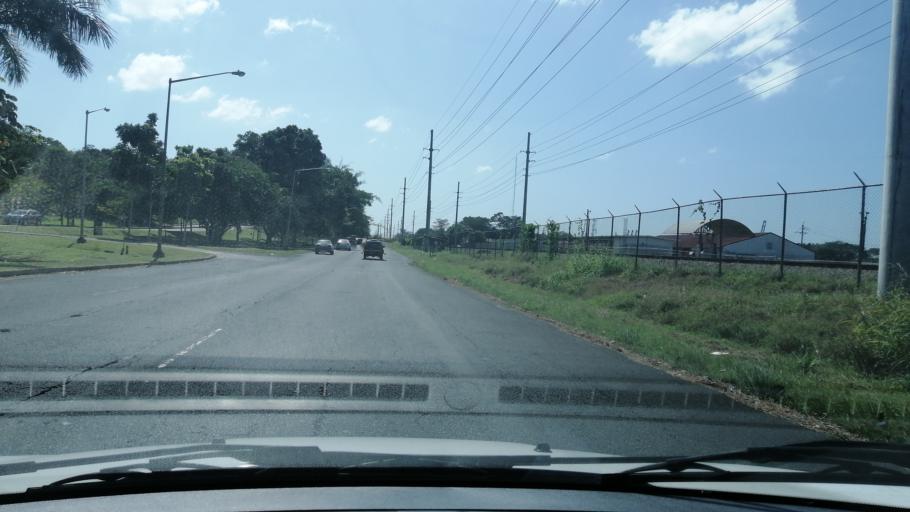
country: PA
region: Panama
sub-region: Distrito de Panama
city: Ancon
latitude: 8.9828
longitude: -79.5721
